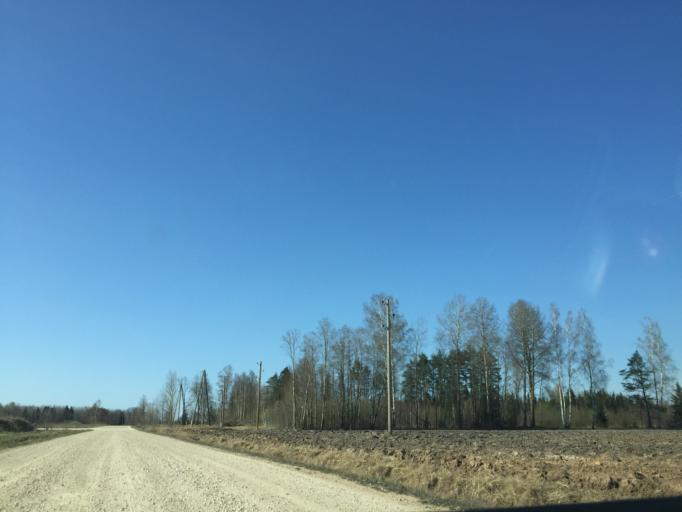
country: LV
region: Ropazu
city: Ropazi
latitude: 56.9452
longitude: 24.7017
